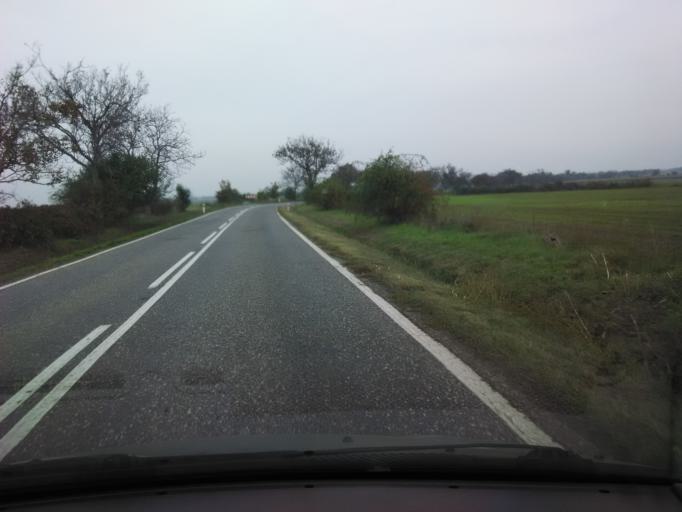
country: SK
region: Nitriansky
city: Svodin
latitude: 48.0527
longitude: 18.4922
